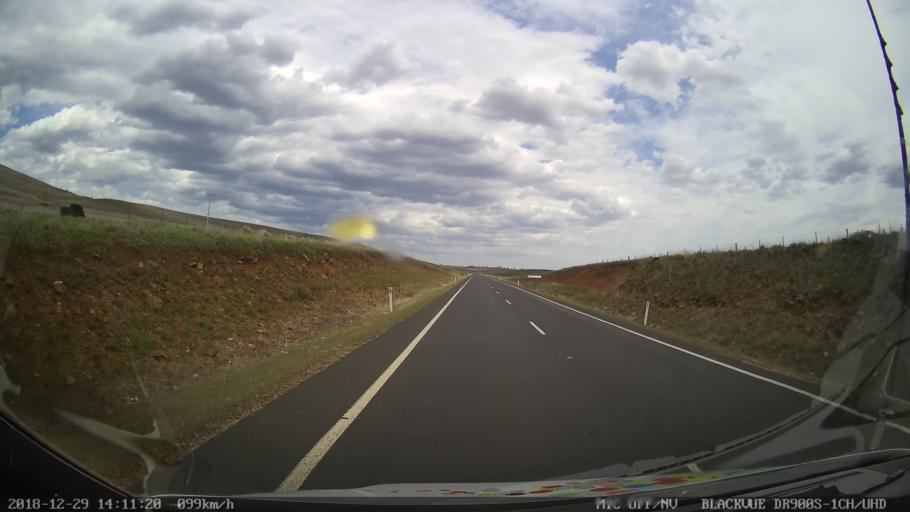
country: AU
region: New South Wales
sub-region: Cooma-Monaro
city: Cooma
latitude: -36.4045
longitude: 149.2197
